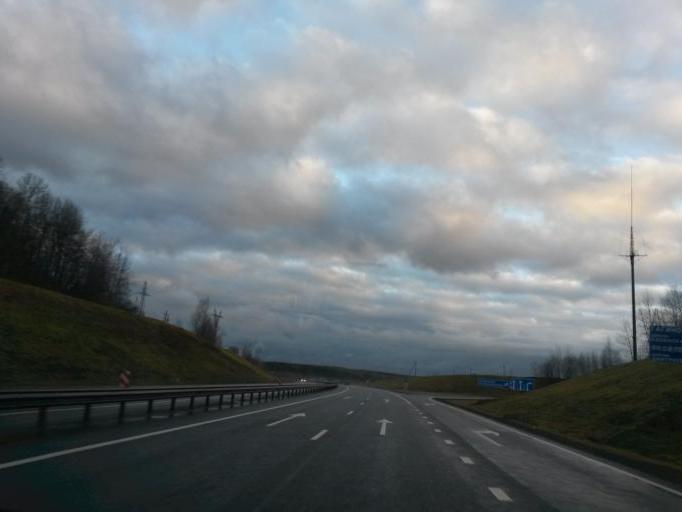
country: RU
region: Moskovskaya
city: Svatkovo
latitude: 56.3799
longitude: 38.3225
